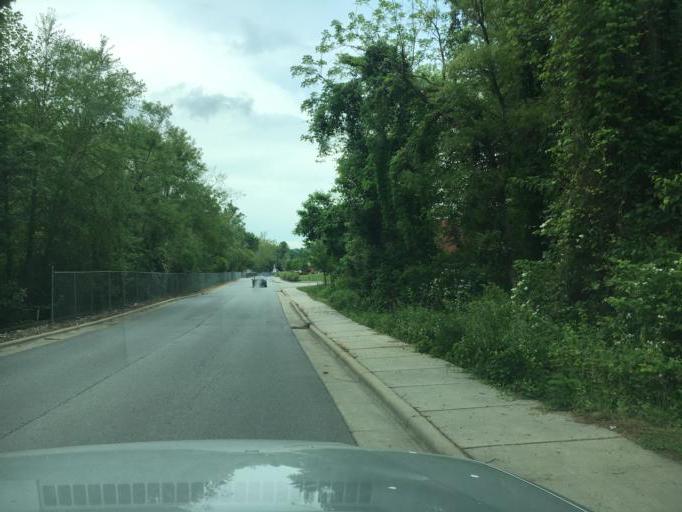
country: US
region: North Carolina
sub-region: Henderson County
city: Hendersonville
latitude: 35.3102
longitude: -82.4546
